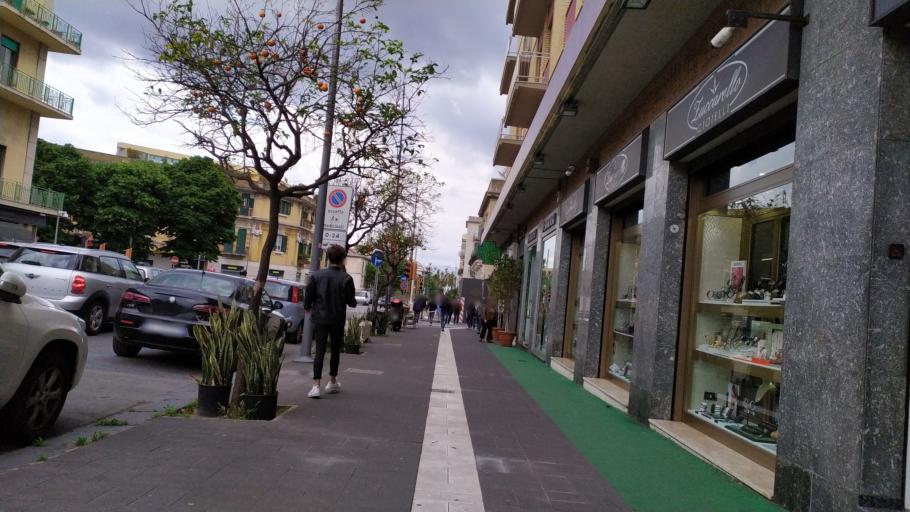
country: IT
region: Sicily
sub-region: Messina
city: Messina
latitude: 38.1871
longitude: 15.5554
